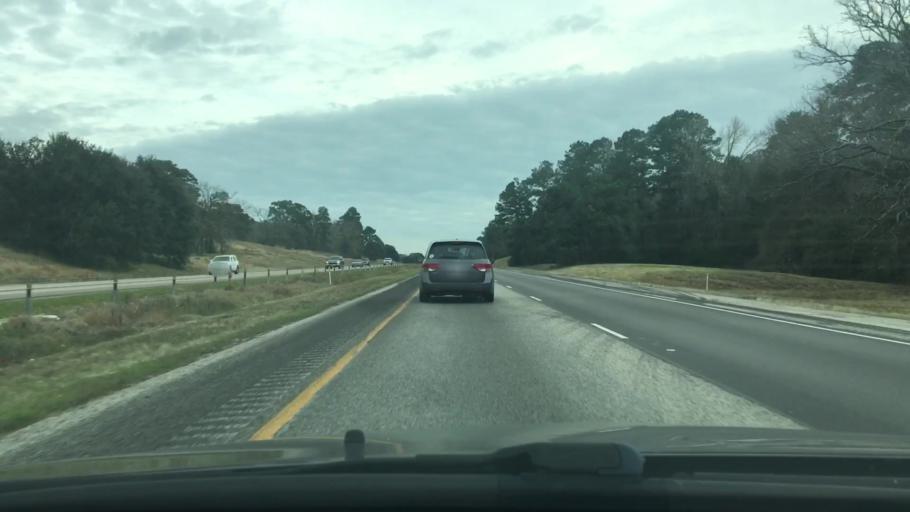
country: US
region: Texas
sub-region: Walker County
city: Huntsville
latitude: 30.8202
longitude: -95.7025
